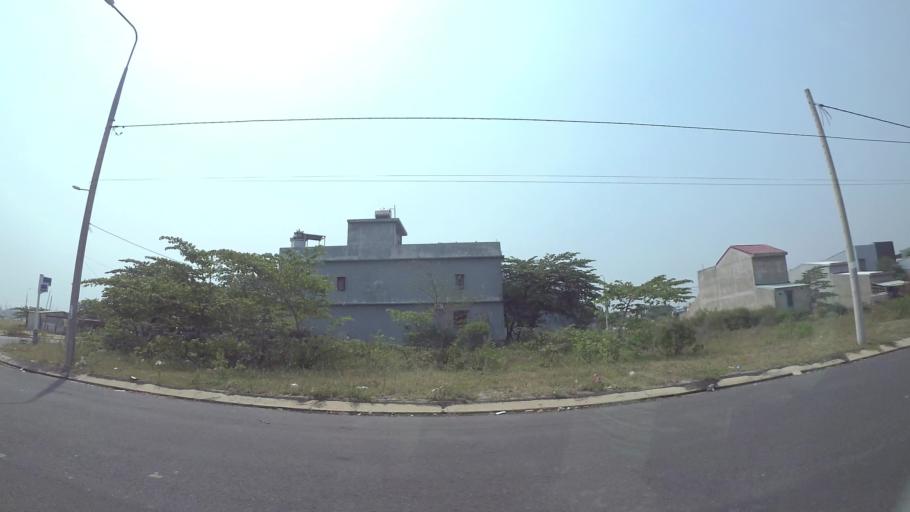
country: VN
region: Da Nang
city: Cam Le
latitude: 15.9830
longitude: 108.2156
